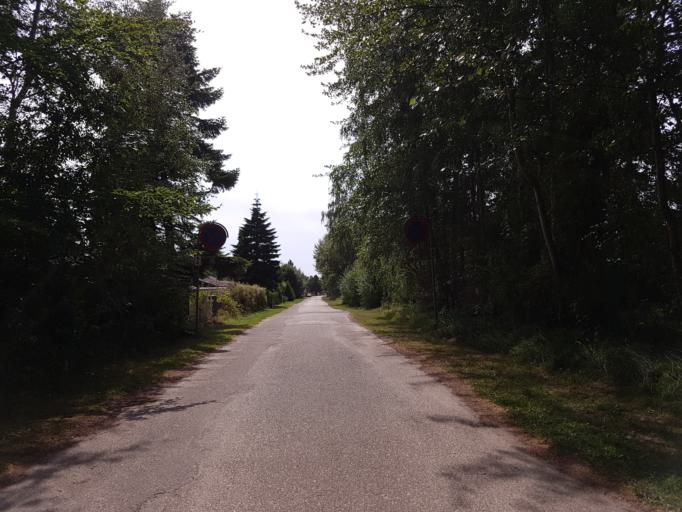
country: DK
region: Zealand
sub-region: Guldborgsund Kommune
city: Nykobing Falster
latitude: 54.6008
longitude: 11.9662
